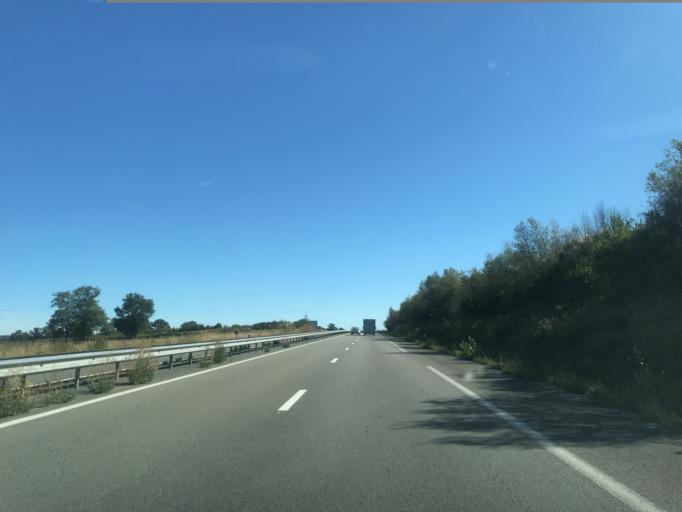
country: FR
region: Limousin
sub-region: Departement de la Creuse
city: Chambon-sur-Voueize
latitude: 46.2771
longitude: 2.3900
